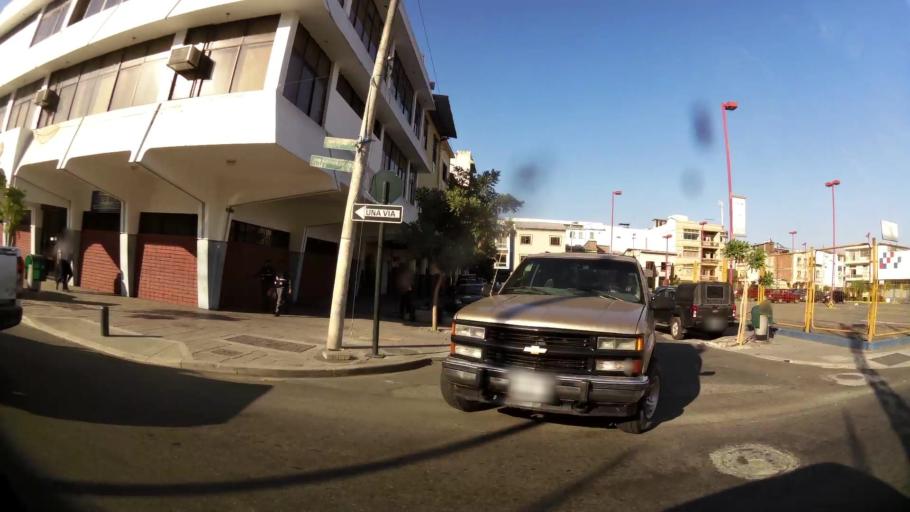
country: EC
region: Guayas
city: Eloy Alfaro
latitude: -2.1848
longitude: -79.8812
